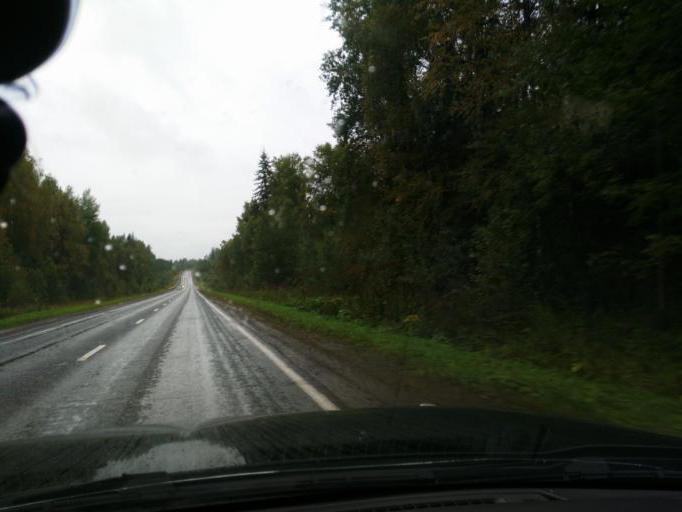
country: RU
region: Perm
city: Yugo-Kamskiy
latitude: 57.6523
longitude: 55.5977
